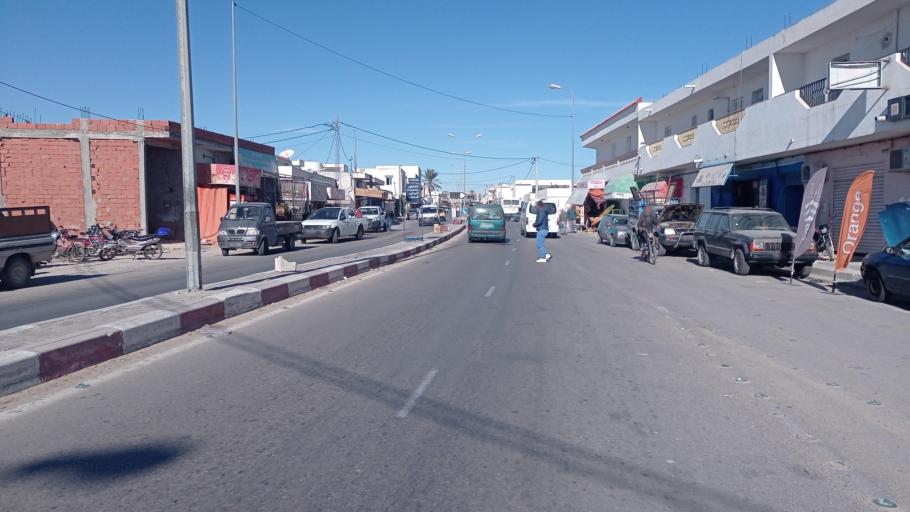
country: TN
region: Qabis
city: Gabes
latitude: 33.8392
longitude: 10.1158
